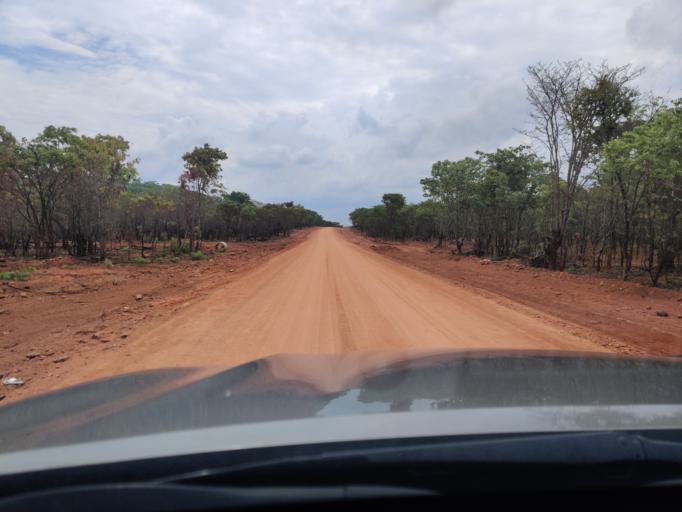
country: ZM
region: Central
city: Mkushi
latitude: -13.8272
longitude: 29.8751
